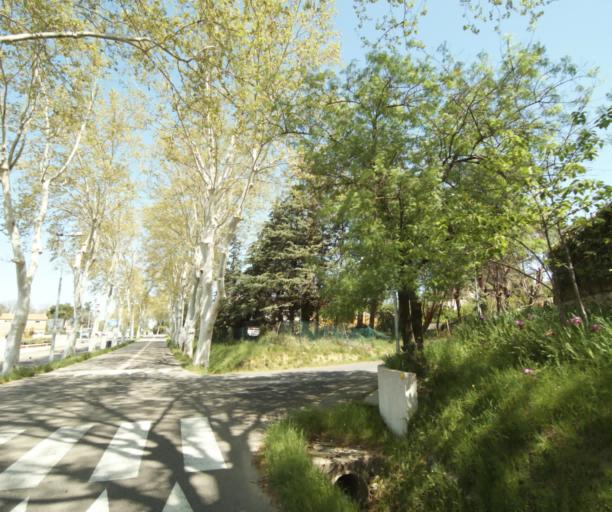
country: FR
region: Languedoc-Roussillon
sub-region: Departement de l'Herault
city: Prades-le-Lez
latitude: 43.6904
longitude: 3.8628
